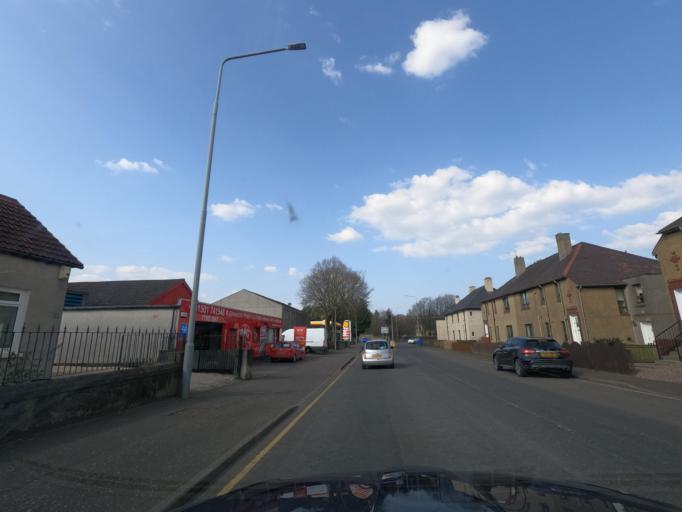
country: GB
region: Scotland
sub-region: West Lothian
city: Whitburn
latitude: 55.8684
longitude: -3.6861
